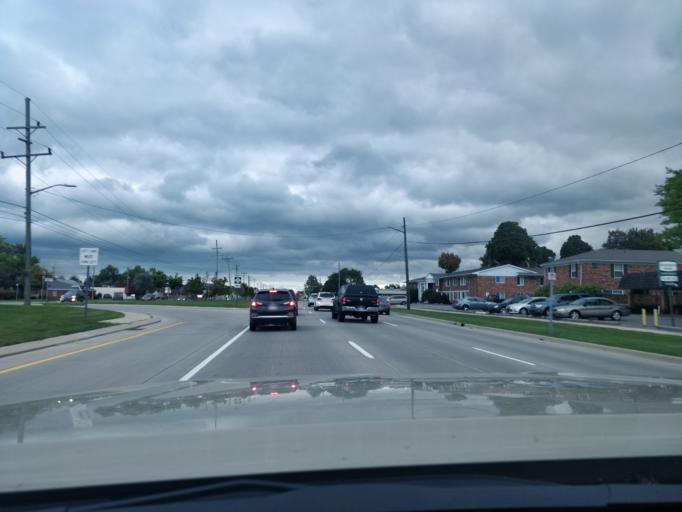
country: US
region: Michigan
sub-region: Wayne County
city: Riverview
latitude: 42.1818
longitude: -83.1898
